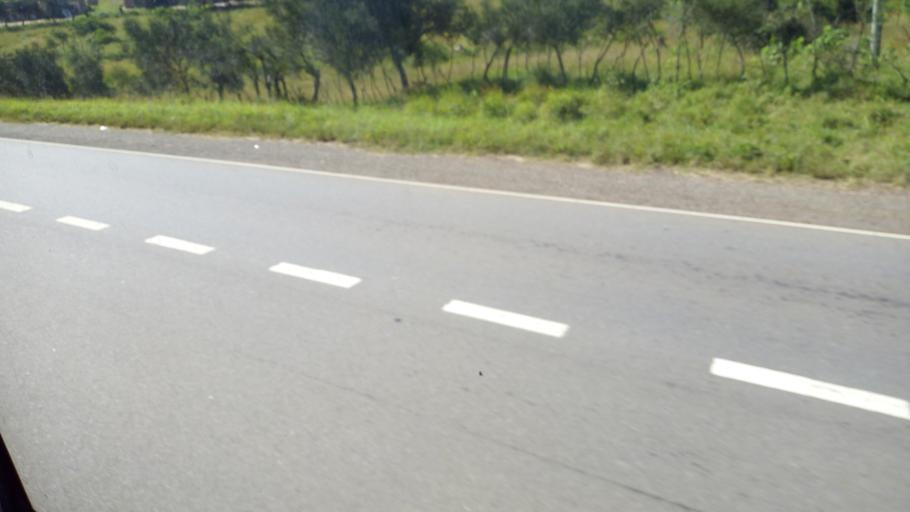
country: UG
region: Central Region
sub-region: Lyantonde District
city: Lyantonde
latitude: -0.4408
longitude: 31.0784
